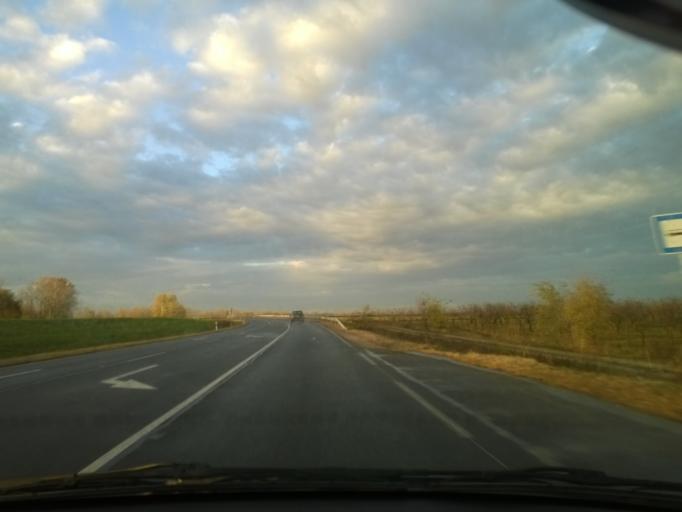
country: HU
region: Bacs-Kiskun
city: Harta
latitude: 46.7305
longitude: 19.0159
